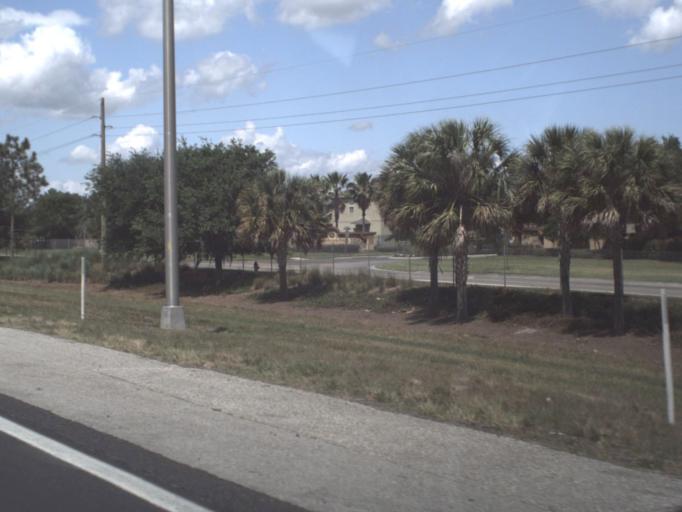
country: US
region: Florida
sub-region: Orange County
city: Winter Garden
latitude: 28.5154
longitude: -81.5958
